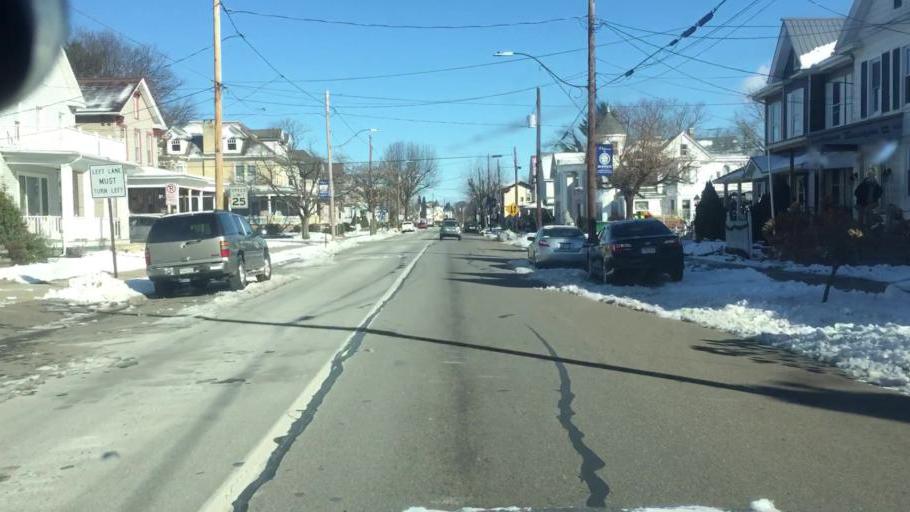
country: US
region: Pennsylvania
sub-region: Columbia County
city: Berwick
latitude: 41.0561
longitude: -76.2308
